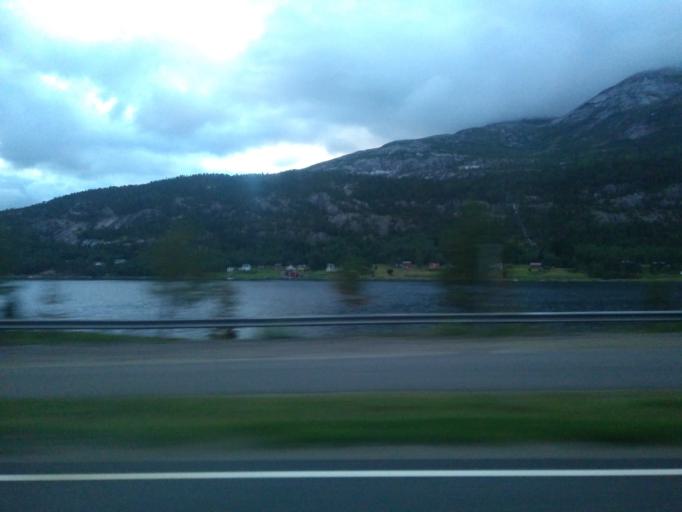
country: NO
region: Nordland
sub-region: Sorfold
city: Straumen
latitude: 67.7047
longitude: 15.8471
